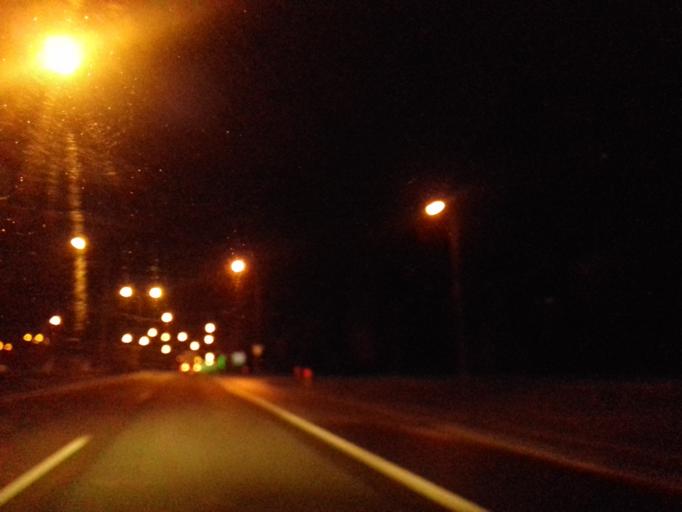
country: CZ
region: South Moravian
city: Ostopovice
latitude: 49.1776
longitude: 16.5635
